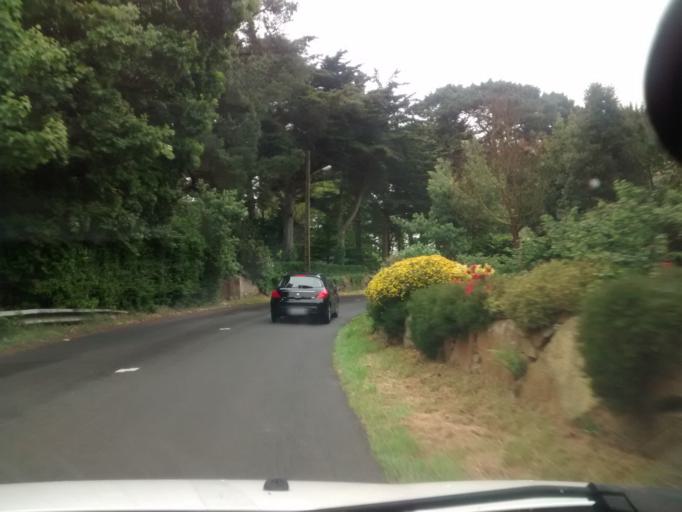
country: FR
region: Brittany
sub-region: Departement des Cotes-d'Armor
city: Penvenan
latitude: 48.8343
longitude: -3.3067
